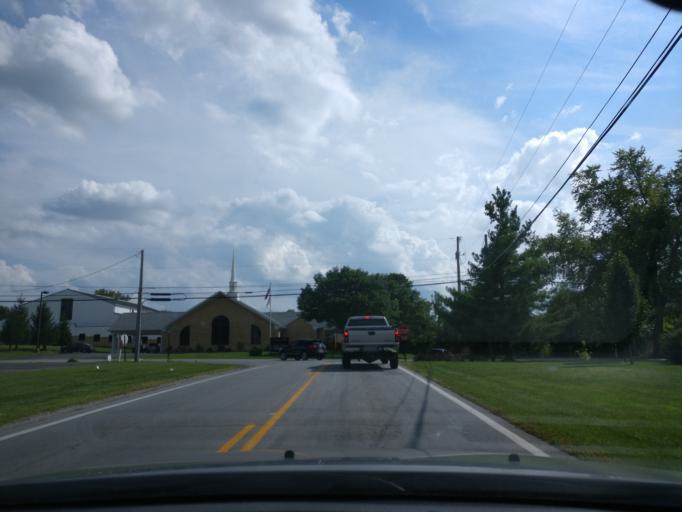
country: US
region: Ohio
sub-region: Warren County
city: Waynesville
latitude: 39.5810
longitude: -84.1046
